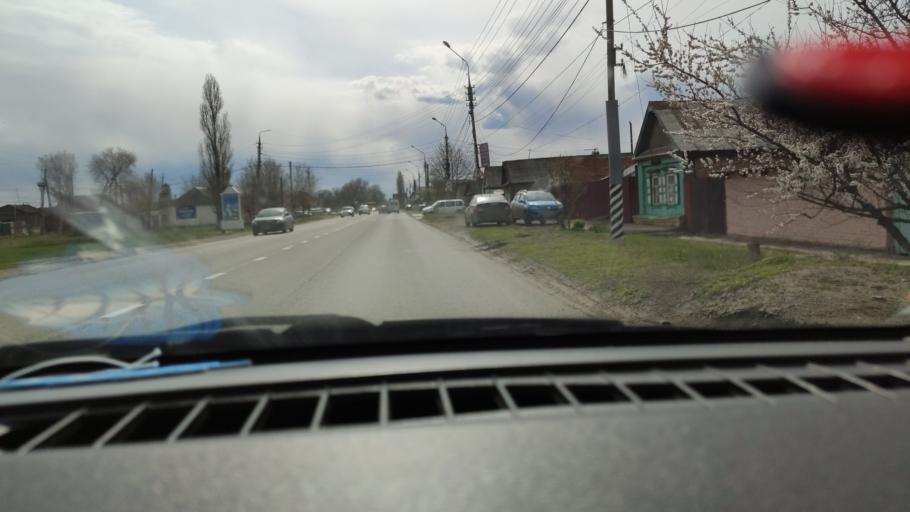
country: RU
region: Saratov
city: Privolzhskiy
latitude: 51.4252
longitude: 46.0463
